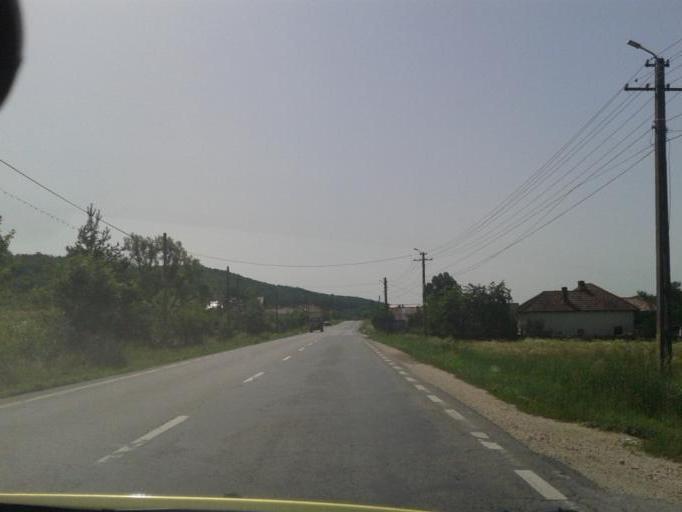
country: RO
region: Arges
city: Draganu-Olteni
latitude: 44.9271
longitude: 24.7149
